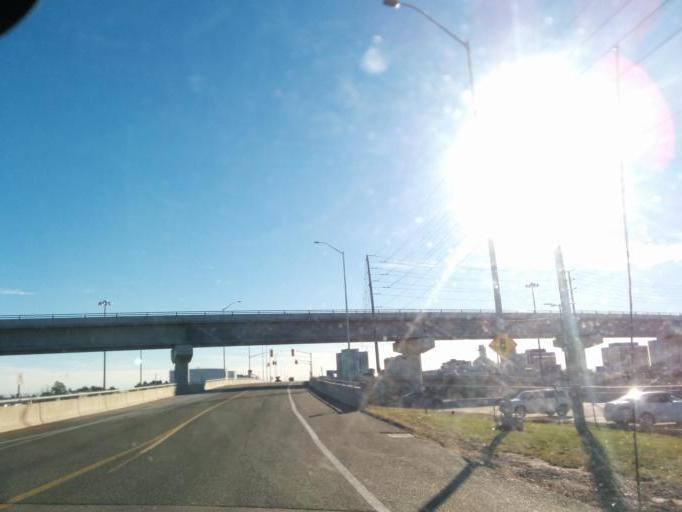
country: CA
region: Ontario
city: Etobicoke
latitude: 43.6951
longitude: -79.6127
